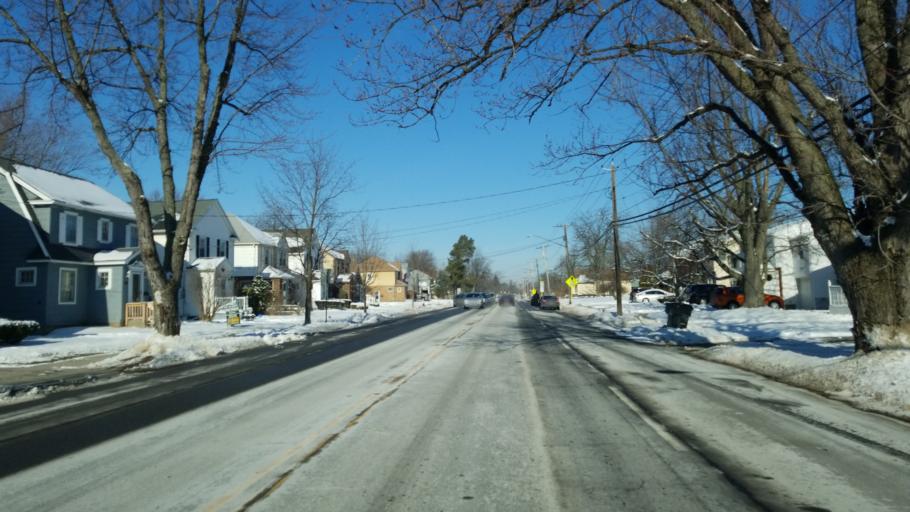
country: US
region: New York
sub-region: Erie County
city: Tonawanda
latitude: 42.9925
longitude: -78.8428
